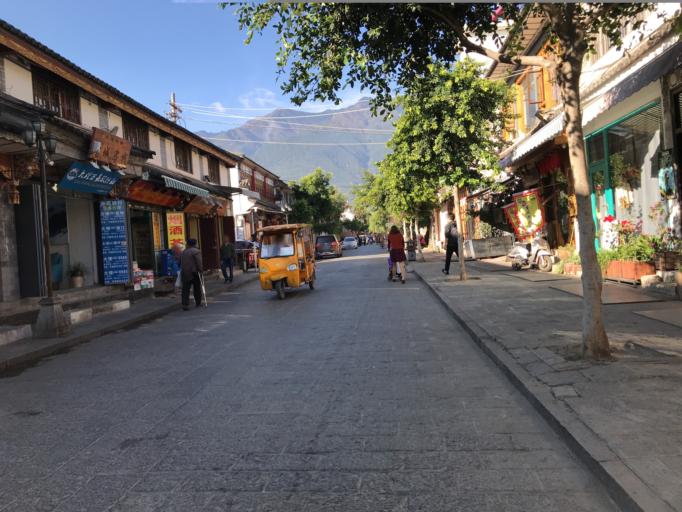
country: CN
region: Yunnan
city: Dali
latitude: 25.6988
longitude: 100.1675
